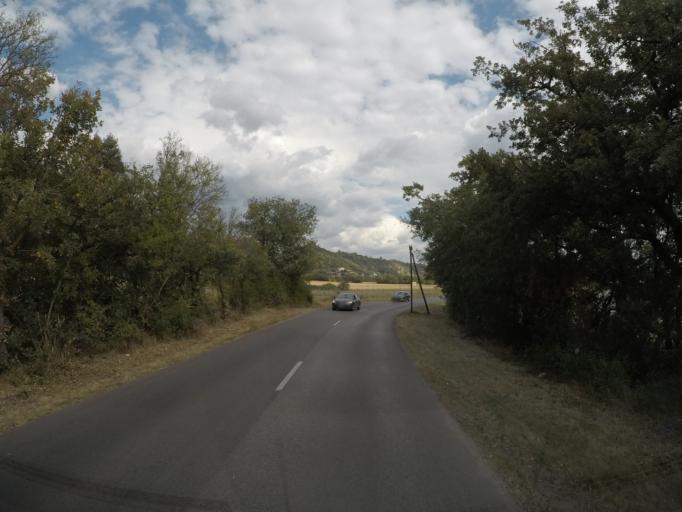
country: FR
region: Provence-Alpes-Cote d'Azur
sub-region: Departement des Alpes-de-Haute-Provence
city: Greoux-les-Bains
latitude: 43.7515
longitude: 5.8543
